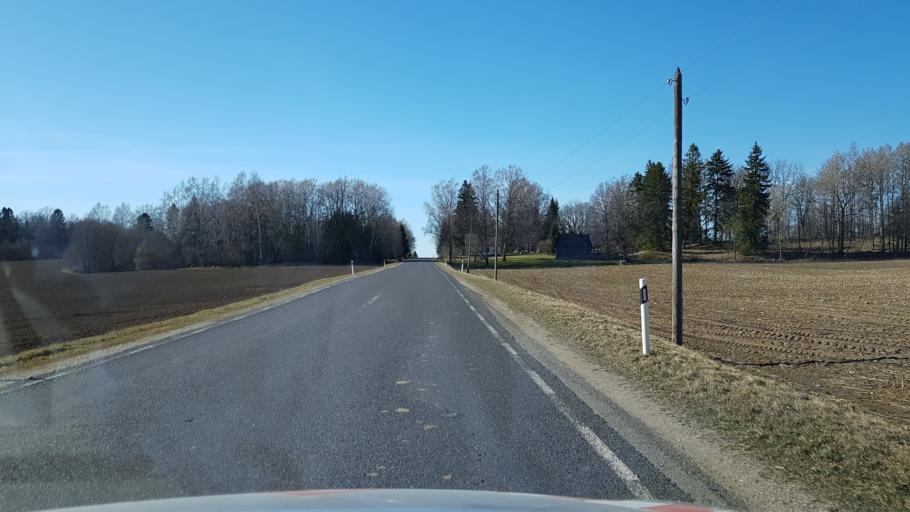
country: EE
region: Laeaene-Virumaa
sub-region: Vinni vald
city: Vinni
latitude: 59.3175
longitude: 26.5115
